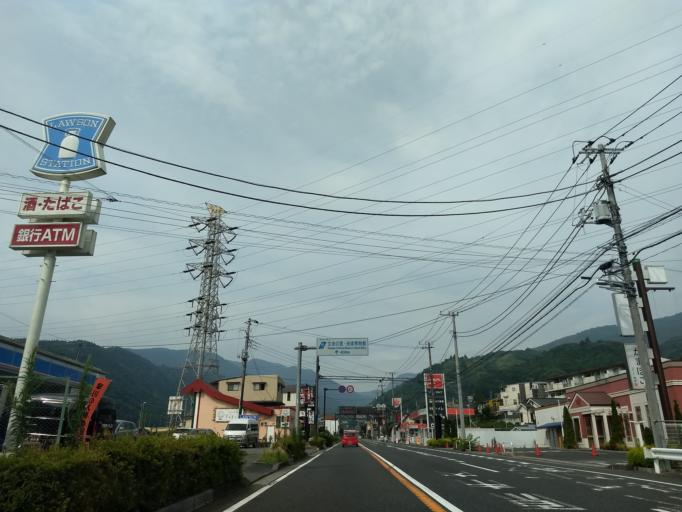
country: JP
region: Kanagawa
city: Odawara
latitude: 35.2435
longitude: 139.1262
